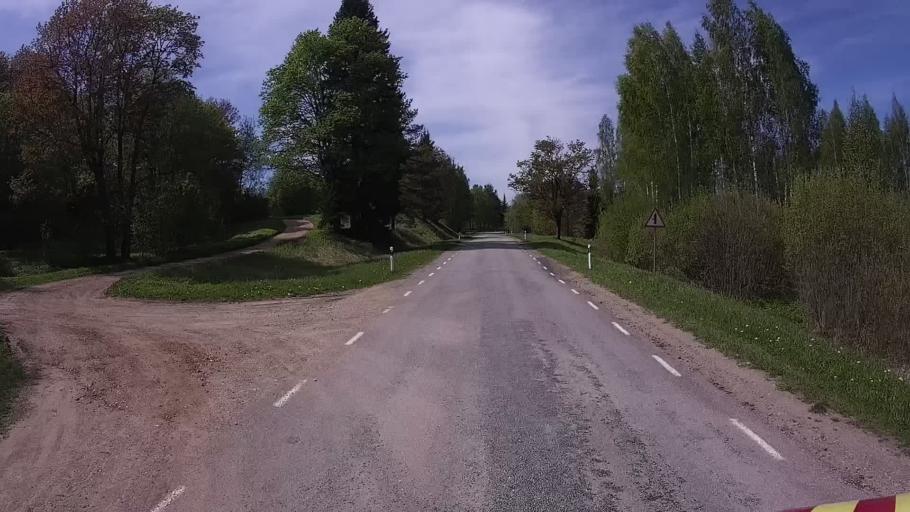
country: EE
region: Valgamaa
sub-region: Valga linn
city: Valga
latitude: 57.6460
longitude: 26.3182
